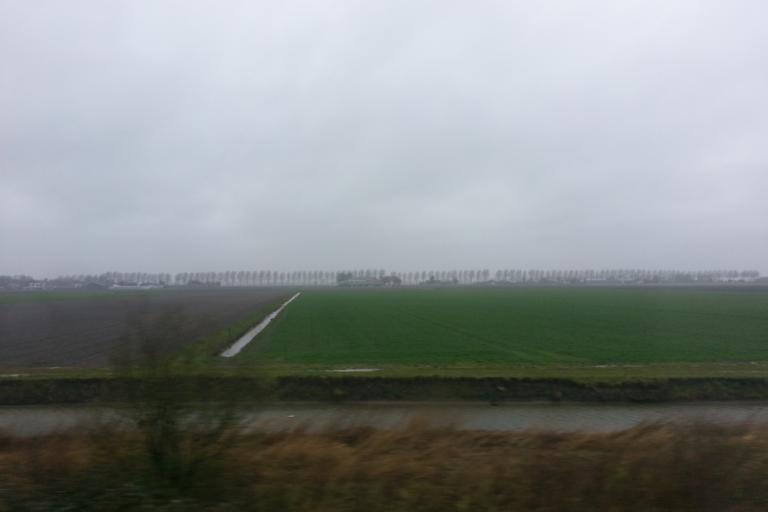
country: NL
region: South Holland
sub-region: Gemeente Kaag en Braassem
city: Oude Wetering
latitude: 52.2329
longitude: 4.6081
